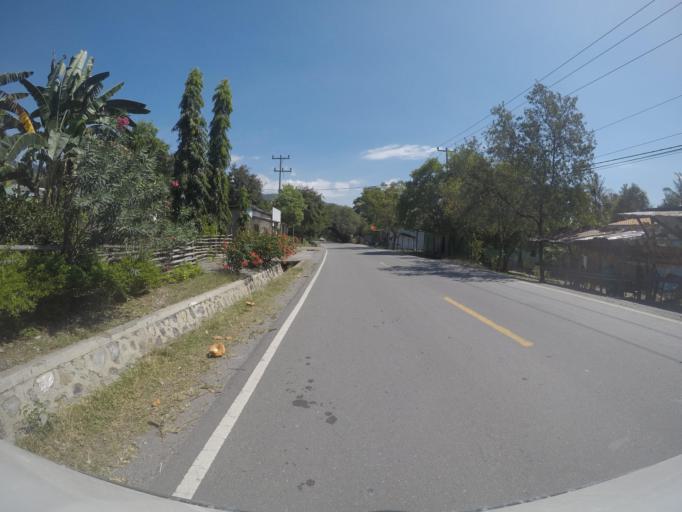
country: TL
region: Liquica
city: Liquica
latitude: -8.5871
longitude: 125.3492
